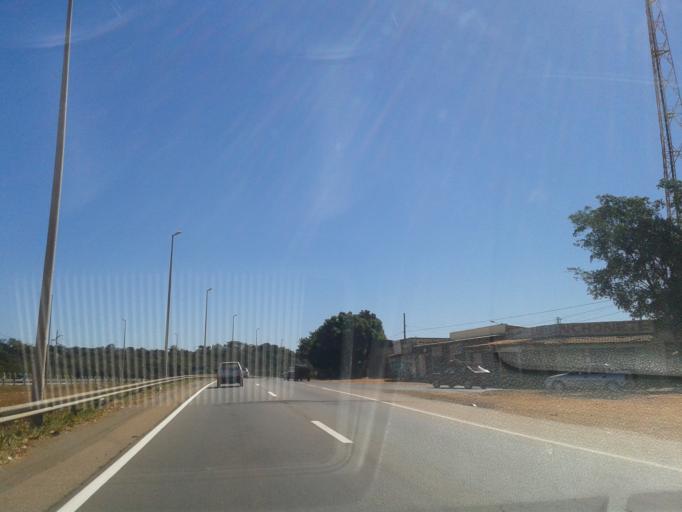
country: BR
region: Goias
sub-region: Goianira
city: Goianira
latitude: -16.5905
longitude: -49.3793
